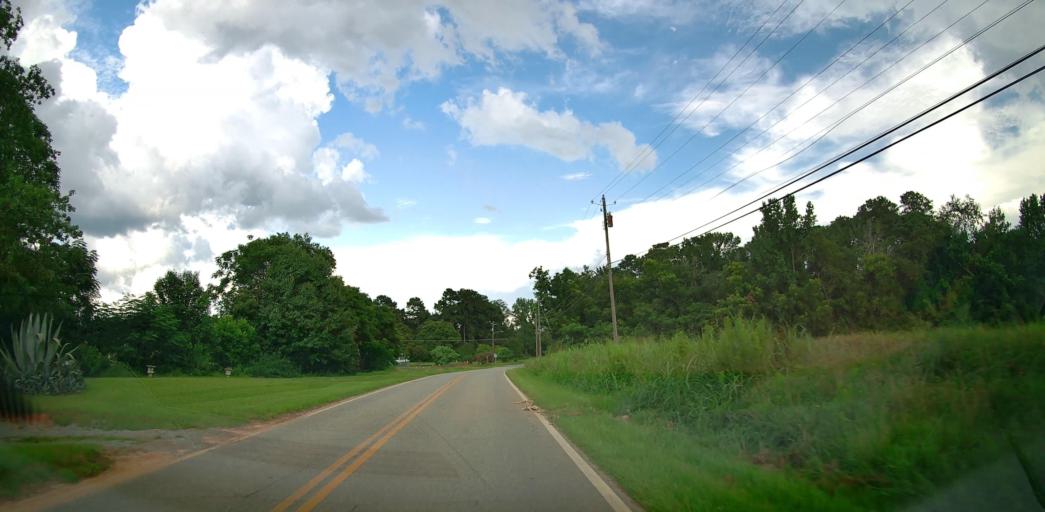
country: US
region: Georgia
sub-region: Bleckley County
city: Cochran
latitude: 32.3942
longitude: -83.3646
